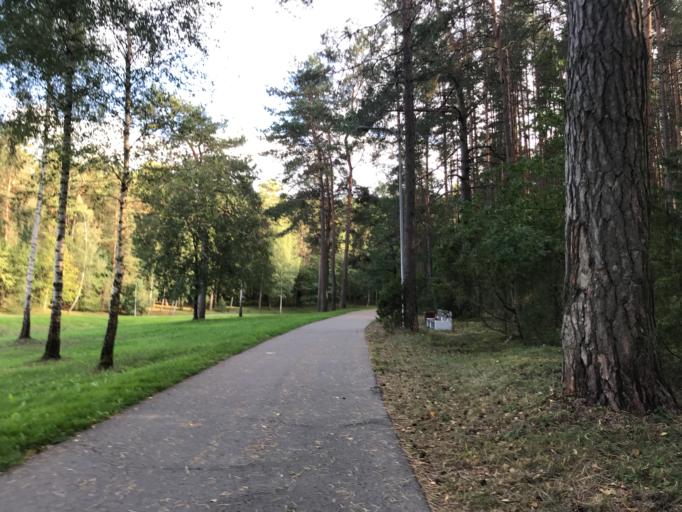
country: LT
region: Alytaus apskritis
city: Druskininkai
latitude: 54.0151
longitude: 23.9603
